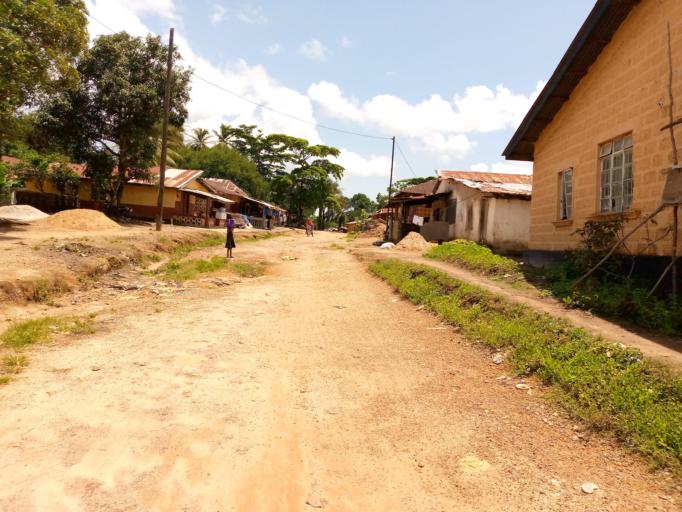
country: SL
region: Northern Province
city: Magburaka
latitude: 8.7163
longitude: -11.9588
